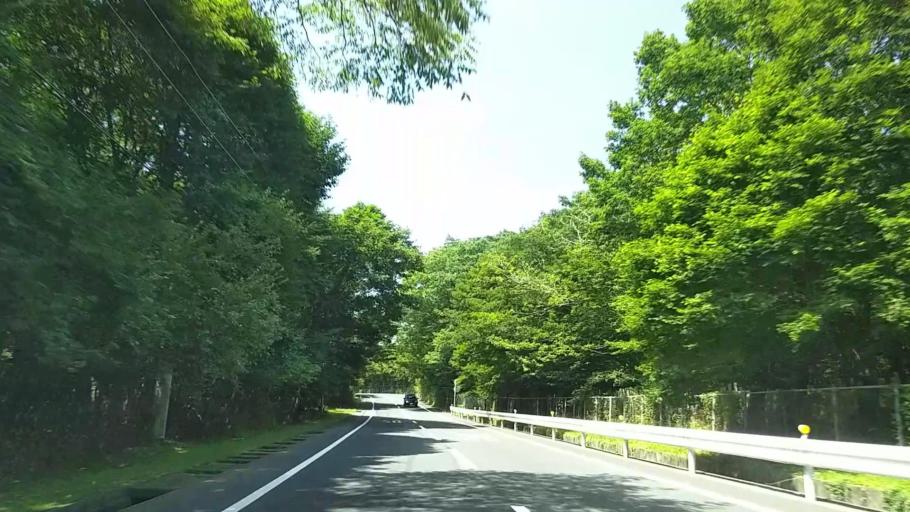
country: JP
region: Shizuoka
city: Gotemba
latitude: 35.2569
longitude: 138.8036
